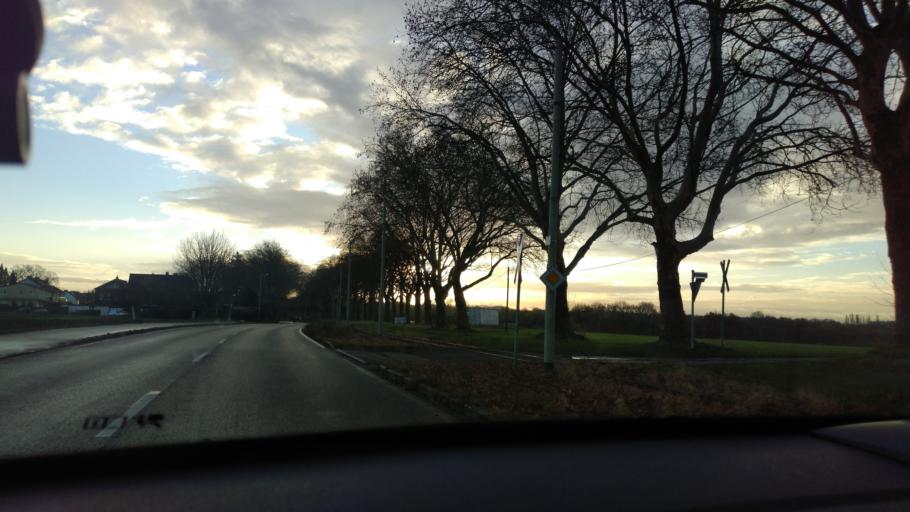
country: DE
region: North Rhine-Westphalia
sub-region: Regierungsbezirk Dusseldorf
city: Muelheim (Ruhr)
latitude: 51.4135
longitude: 6.9218
